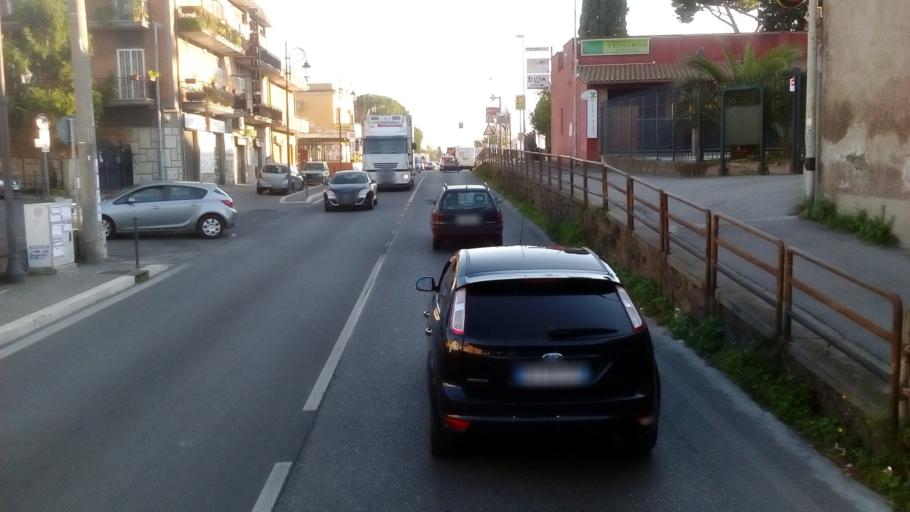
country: IT
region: Latium
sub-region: Citta metropolitana di Roma Capitale
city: Pavona
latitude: 41.7269
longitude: 12.6173
